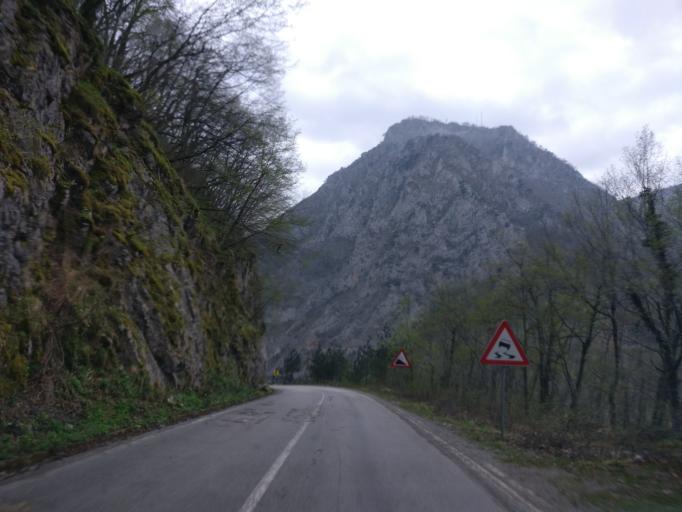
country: ME
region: Opstina Pluzine
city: Pluzine
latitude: 43.2567
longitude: 18.8419
